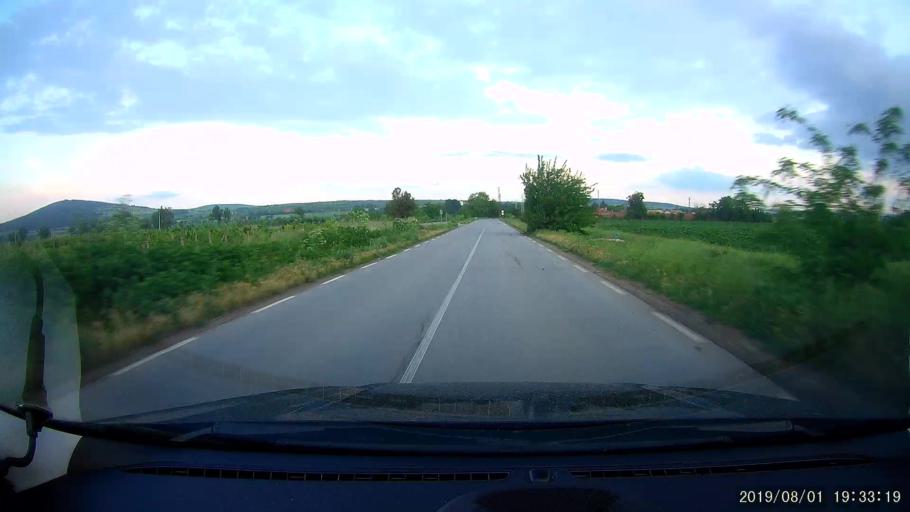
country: BG
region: Burgas
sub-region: Obshtina Sungurlare
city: Sungurlare
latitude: 42.7820
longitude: 26.8758
